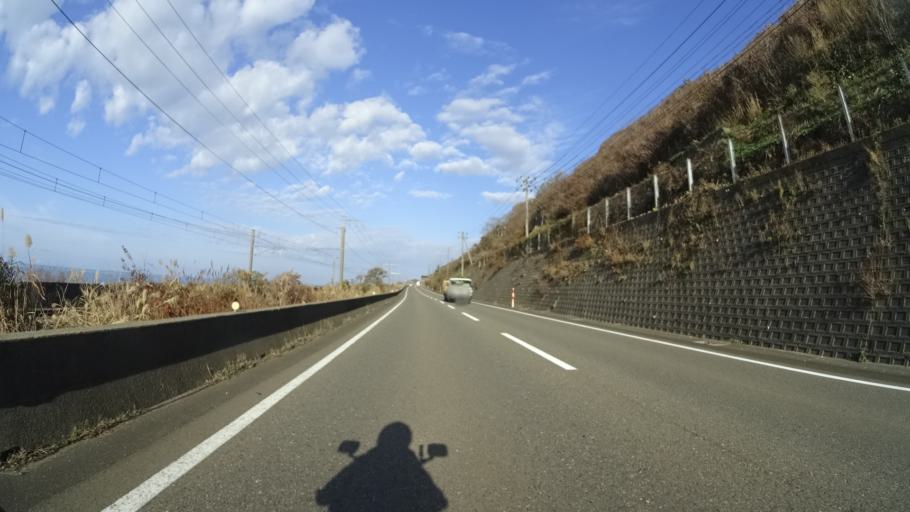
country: JP
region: Niigata
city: Kashiwazaki
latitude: 37.2989
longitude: 138.4108
